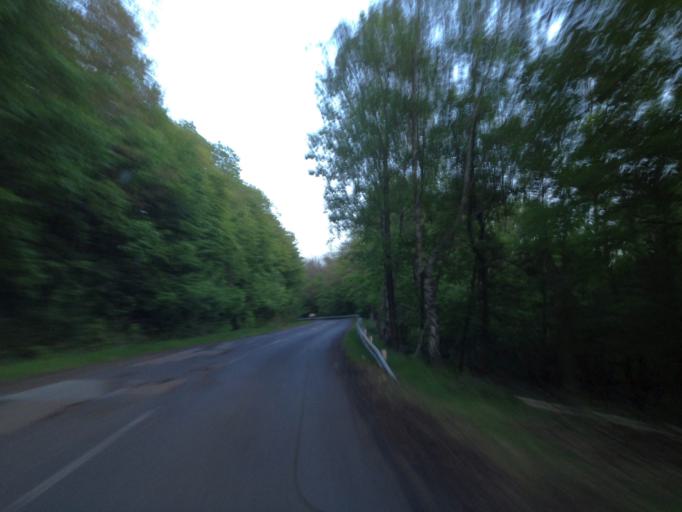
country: HU
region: Heves
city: Gyongyostarjan
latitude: 47.8942
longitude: 19.8691
